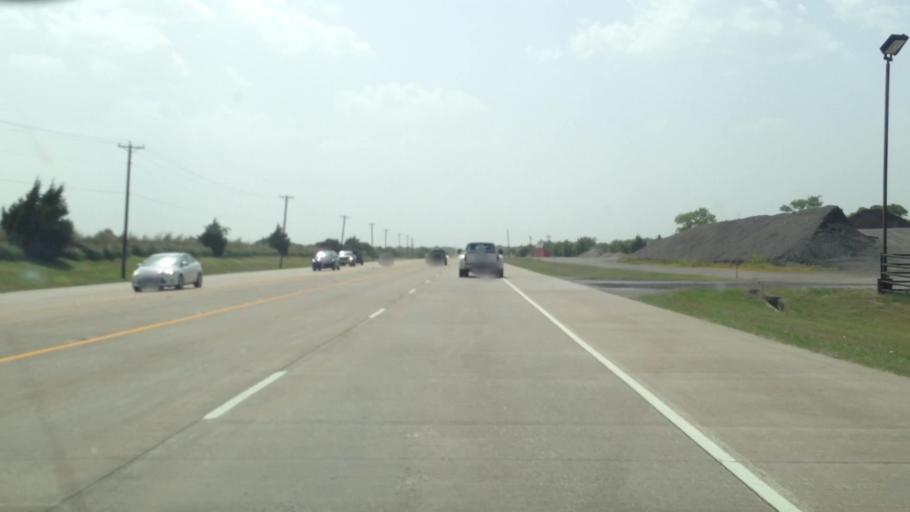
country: US
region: Texas
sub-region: Collin County
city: Princeton
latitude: 33.1674
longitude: -96.4599
